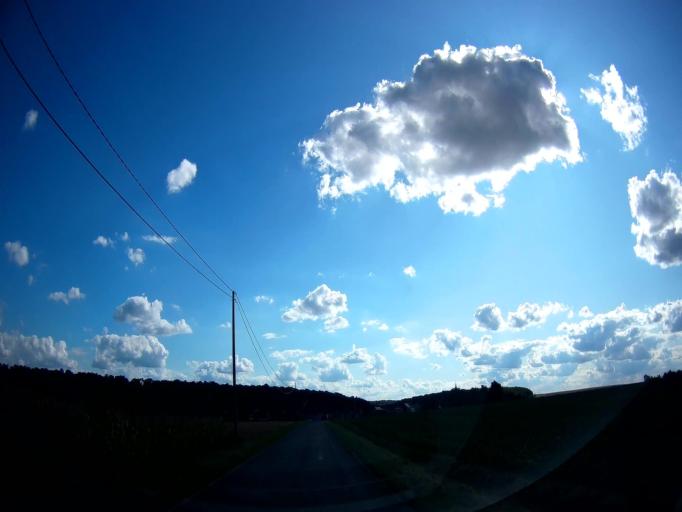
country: BE
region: Wallonia
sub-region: Province de Namur
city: Mettet
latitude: 50.3117
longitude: 4.7112
